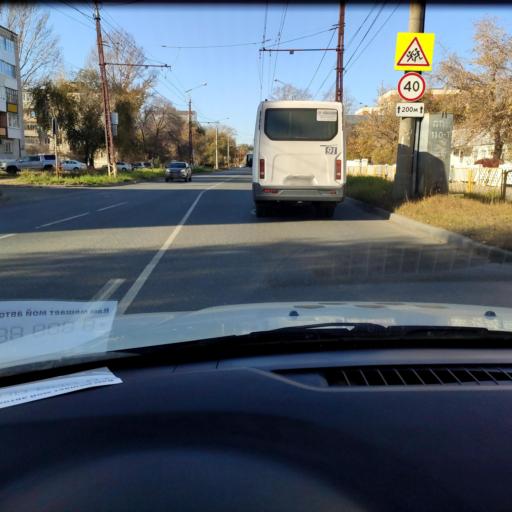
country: RU
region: Samara
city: Tol'yatti
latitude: 53.5211
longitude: 49.4258
